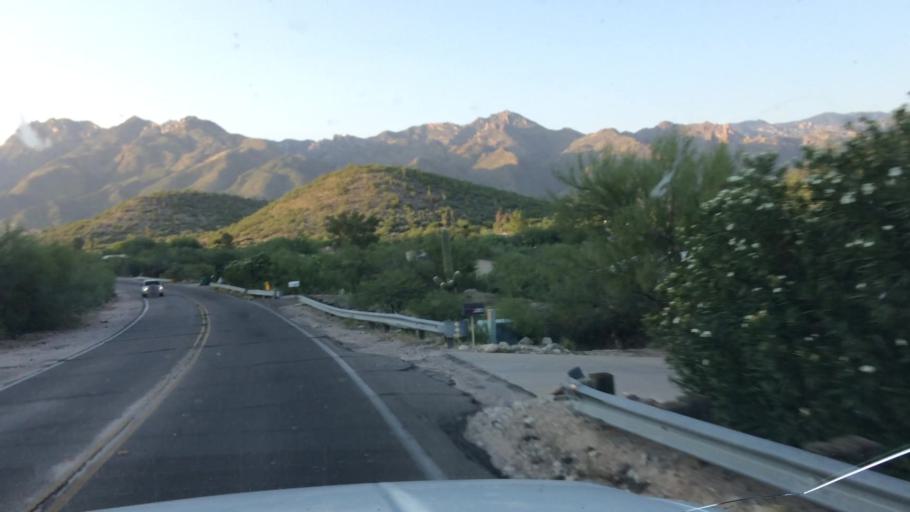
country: US
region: Arizona
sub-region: Pima County
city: Catalina Foothills
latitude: 32.2966
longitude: -110.8394
